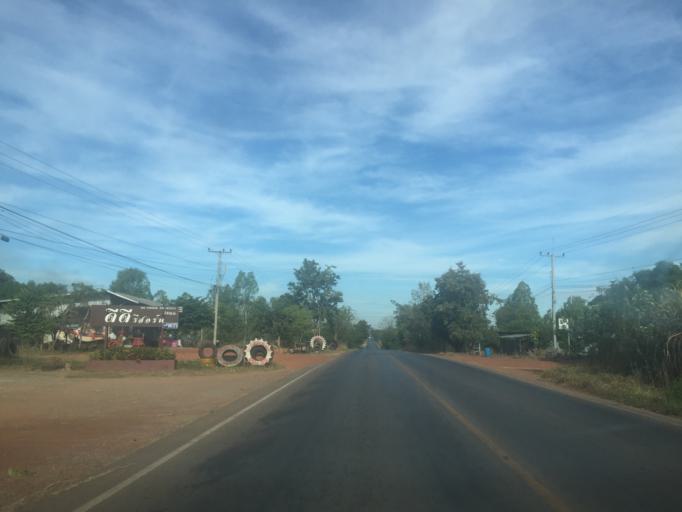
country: TH
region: Changwat Udon Thani
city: Si That
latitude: 16.9937
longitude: 103.1497
